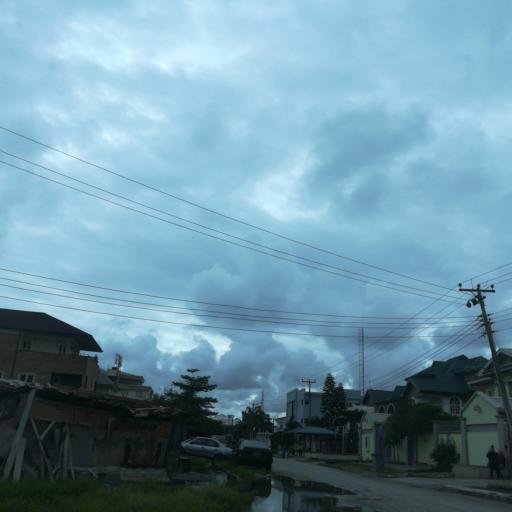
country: NG
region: Lagos
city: Ikoyi
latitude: 6.4409
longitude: 3.4702
